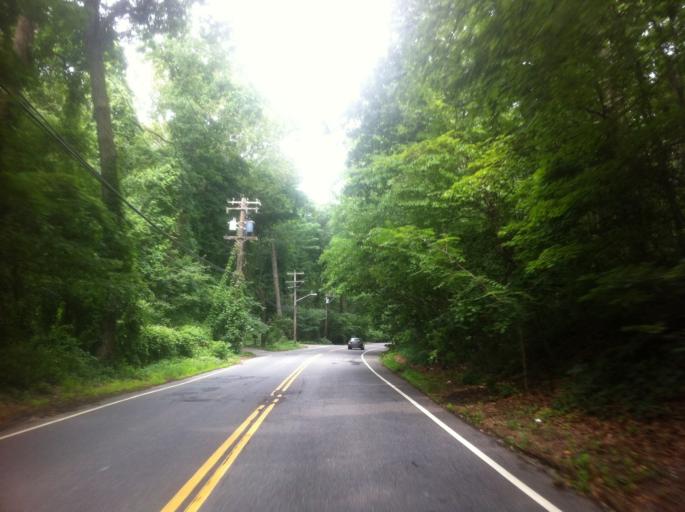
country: US
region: New York
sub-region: Nassau County
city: Oyster Bay Cove
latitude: 40.8570
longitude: -73.5134
